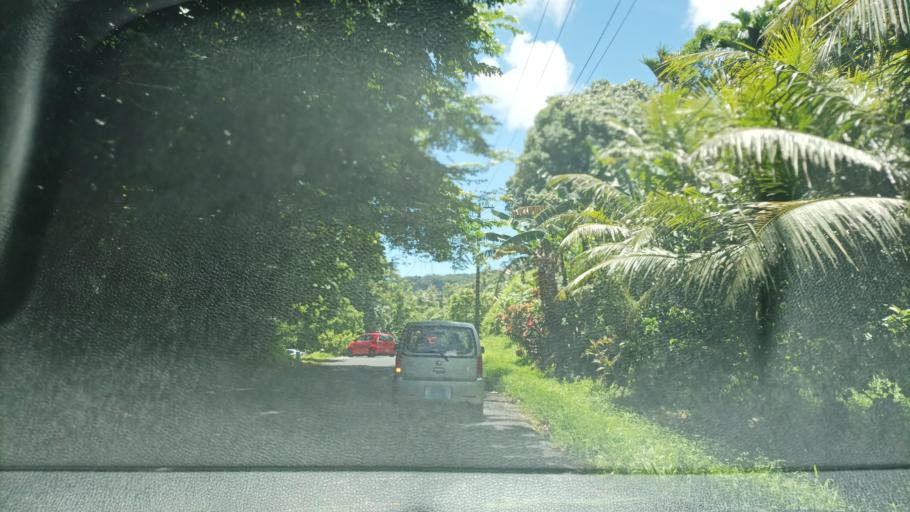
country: FM
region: Pohnpei
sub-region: Kolonia Municipality
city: Kolonia
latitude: 6.9516
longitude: 158.2368
